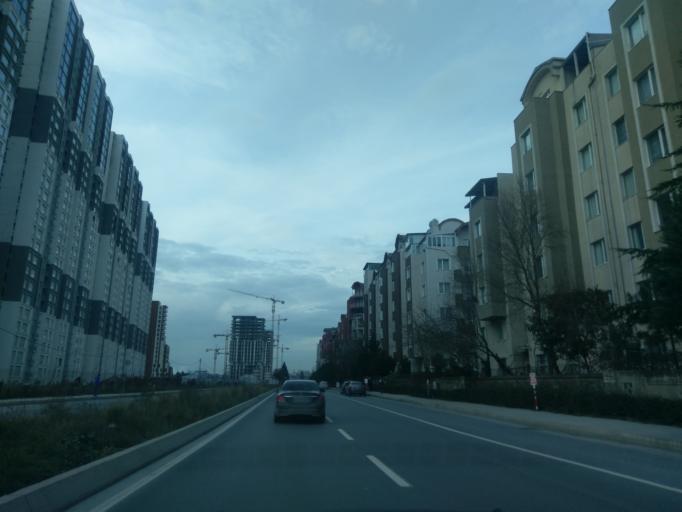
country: TR
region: Istanbul
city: Esenyurt
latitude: 41.0710
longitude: 28.6633
